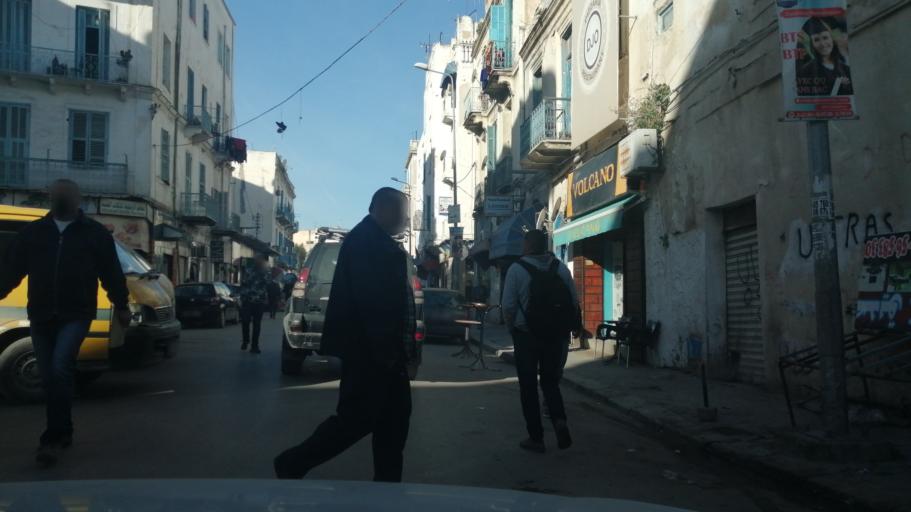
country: TN
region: Tunis
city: Tunis
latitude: 36.8056
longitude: 10.1750
